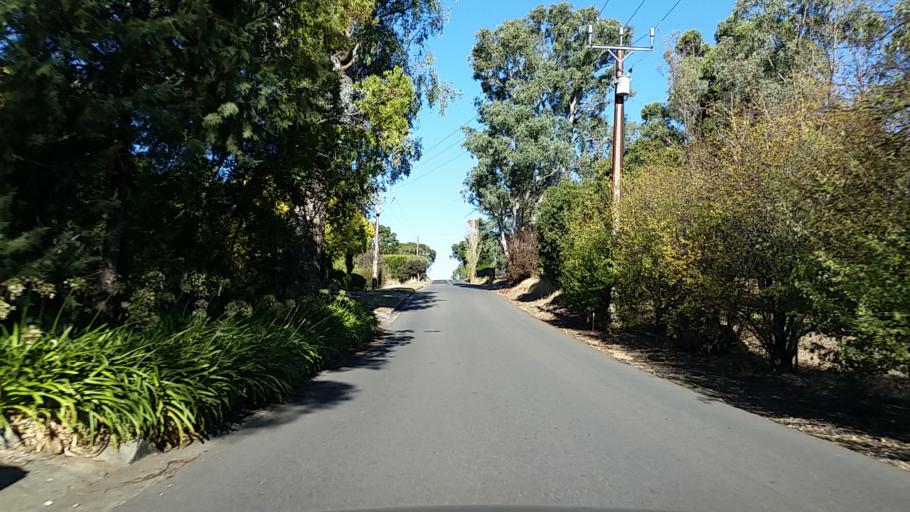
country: AU
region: South Australia
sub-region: Mount Barker
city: Nairne
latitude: -35.0410
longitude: 138.9175
